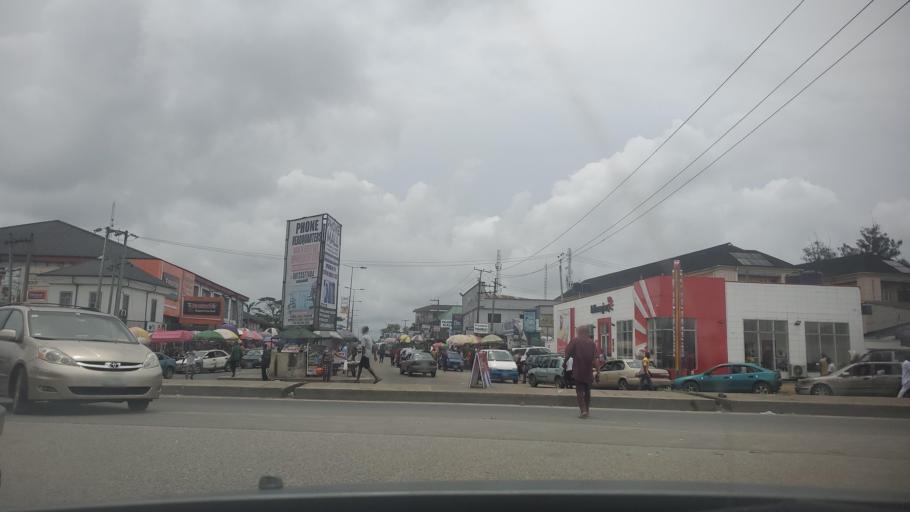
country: NG
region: Rivers
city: Emuoha
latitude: 4.8989
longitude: 6.9068
